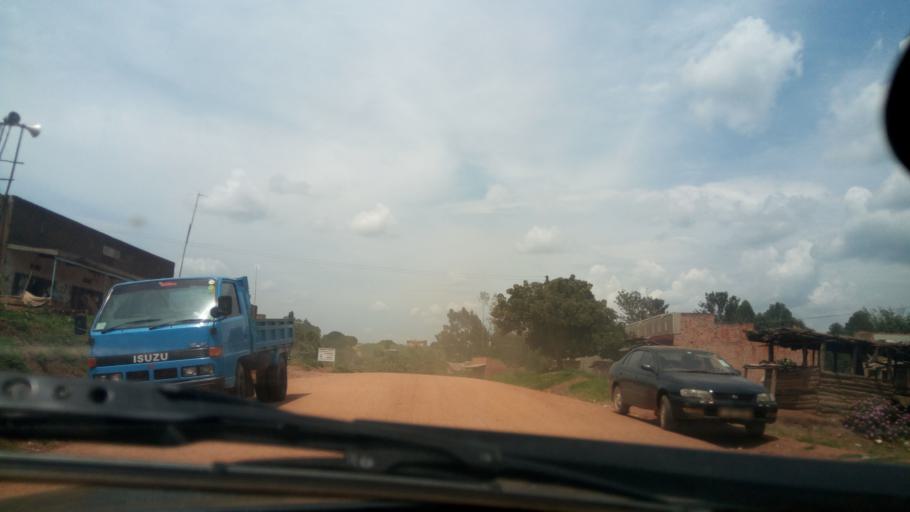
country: UG
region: Central Region
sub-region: Mityana District
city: Mityana
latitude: 0.4484
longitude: 32.0809
